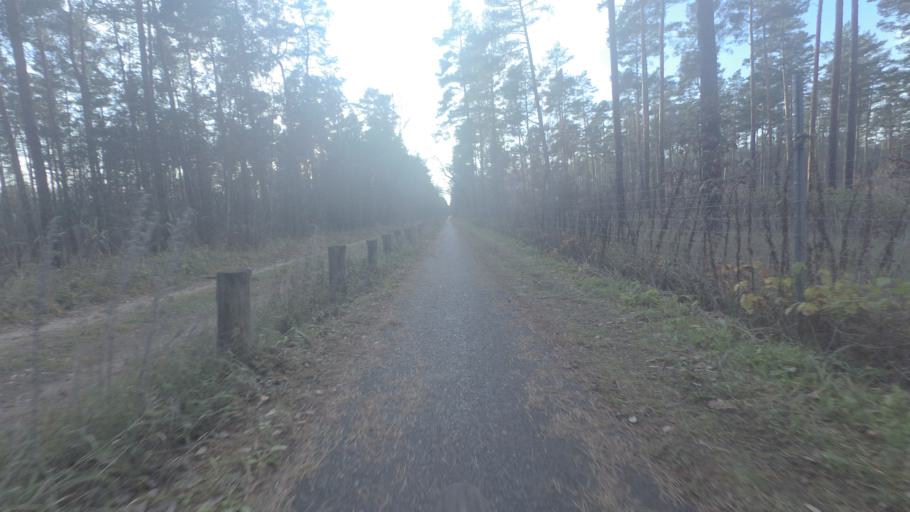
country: DE
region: Brandenburg
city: Mittenwalde
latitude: 52.2000
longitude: 13.5433
